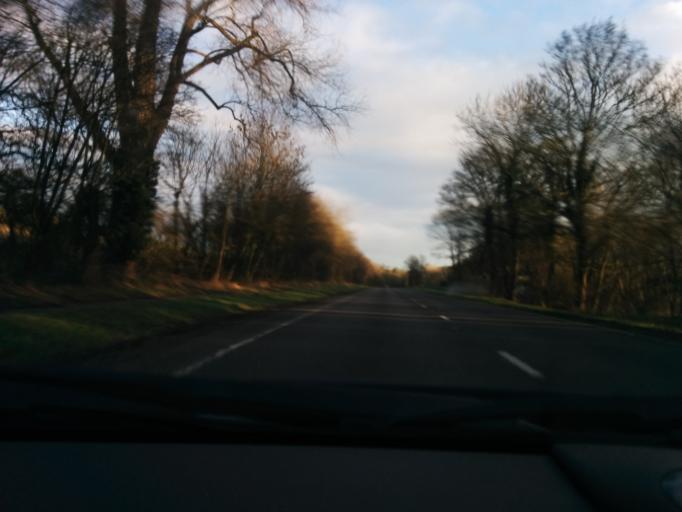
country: GB
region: England
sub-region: Oxfordshire
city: Wheatley
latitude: 51.7593
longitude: -1.1542
